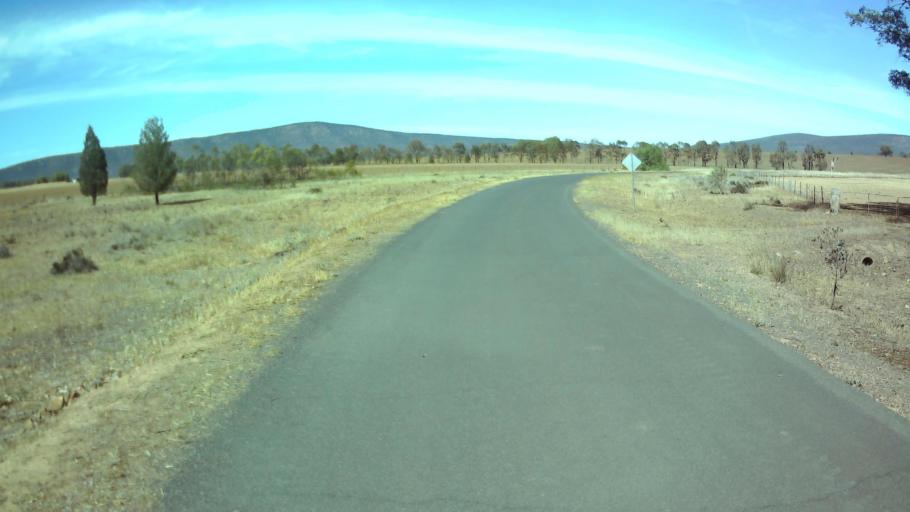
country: AU
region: New South Wales
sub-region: Weddin
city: Grenfell
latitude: -33.9405
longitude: 148.0780
